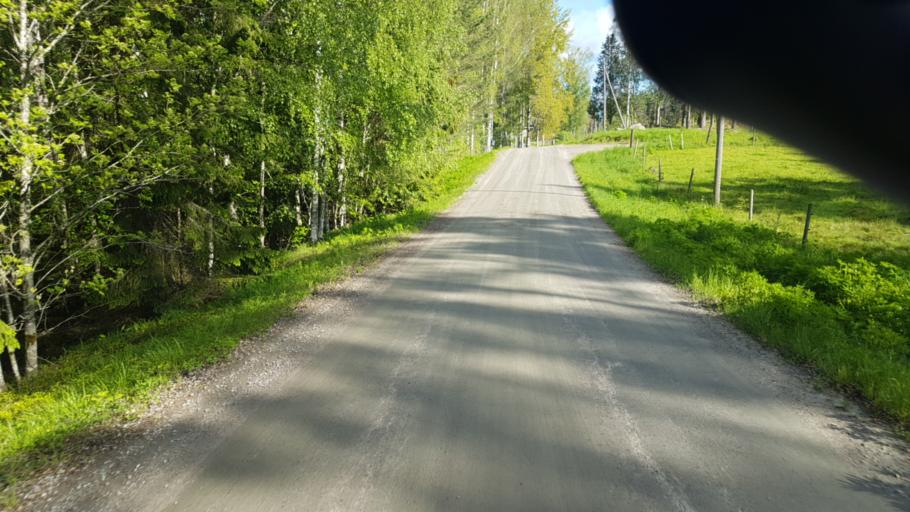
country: SE
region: Vaermland
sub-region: Arvika Kommun
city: Arvika
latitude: 59.5764
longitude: 12.7380
